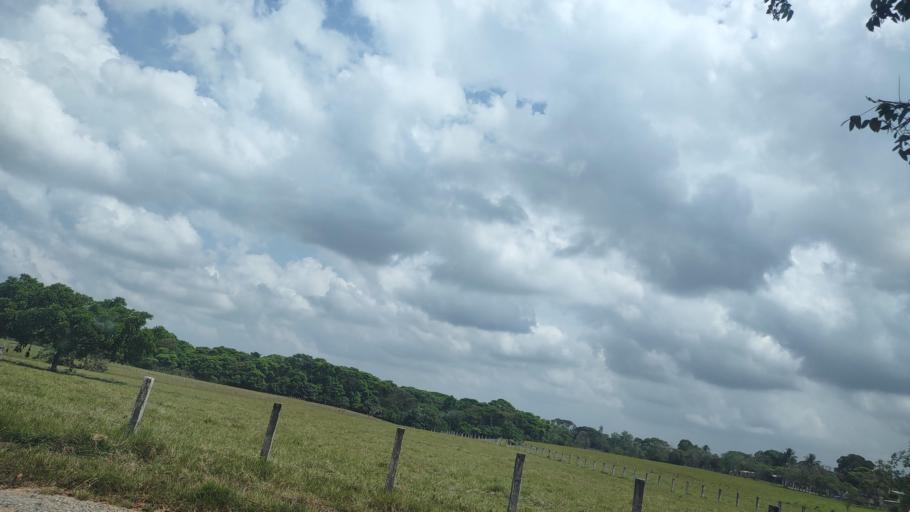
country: MX
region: Veracruz
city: Las Choapas
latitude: 17.9481
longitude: -94.1113
